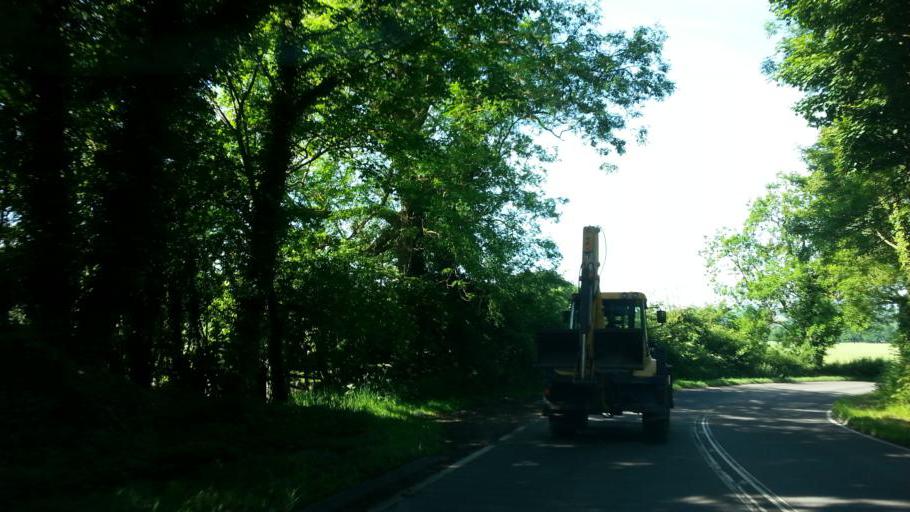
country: GB
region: England
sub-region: Nottinghamshire
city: Farnsfield
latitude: 53.0603
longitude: -1.0423
